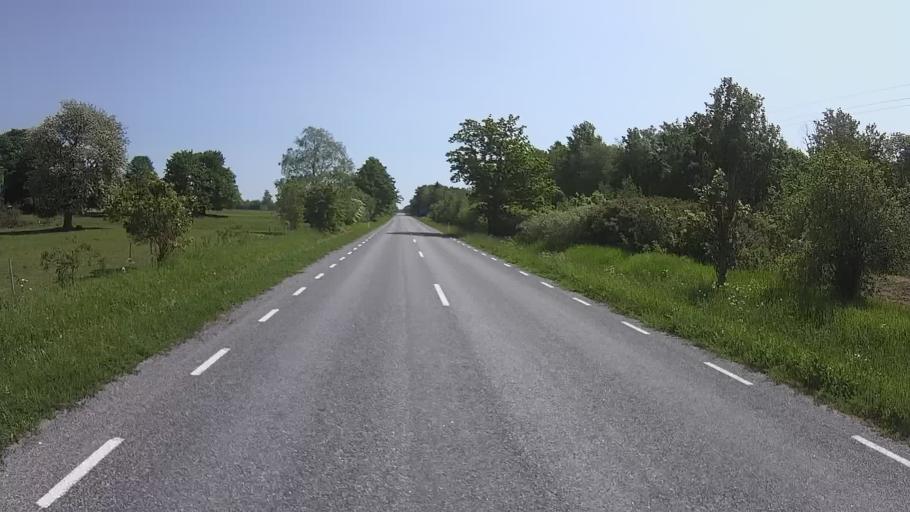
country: EE
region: Saare
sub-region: Kuressaare linn
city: Kuressaare
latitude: 58.3679
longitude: 22.0505
